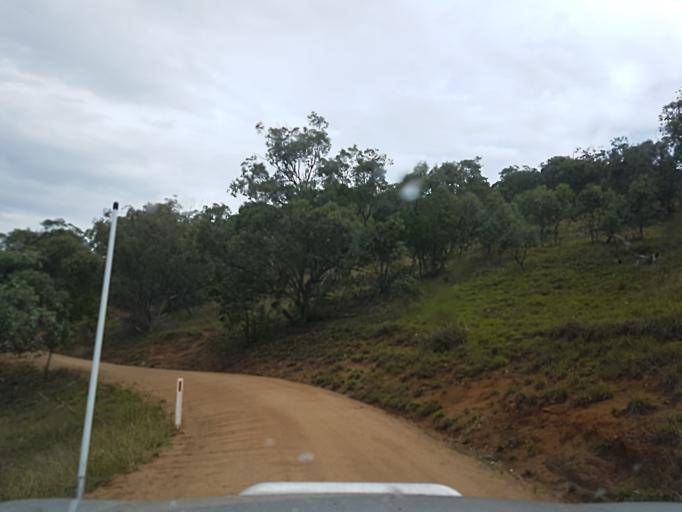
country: AU
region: New South Wales
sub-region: Snowy River
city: Jindabyne
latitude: -36.9470
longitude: 148.3467
